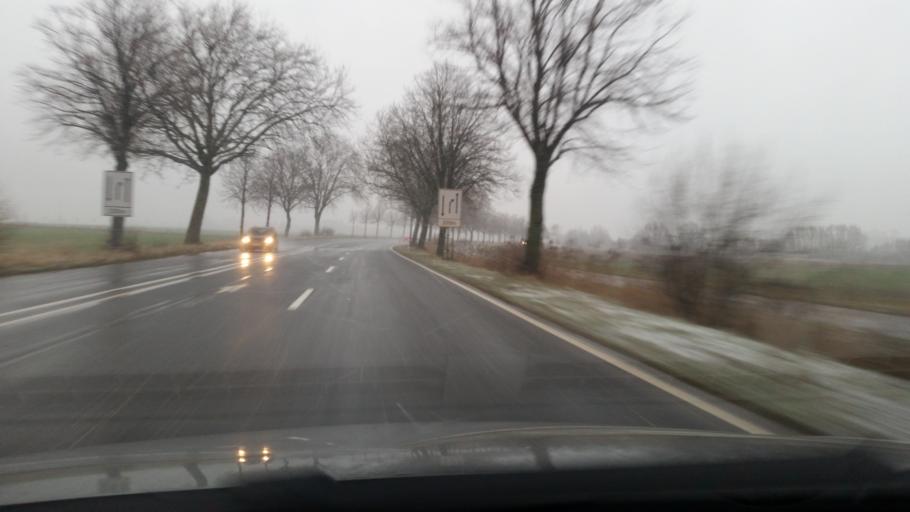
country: DE
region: Lower Saxony
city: Wennigsen
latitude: 52.2521
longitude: 9.6333
